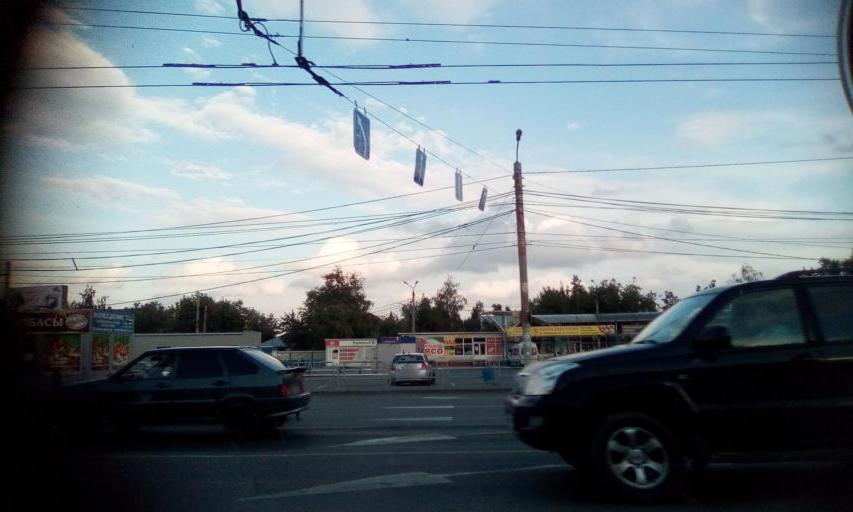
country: RU
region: Chelyabinsk
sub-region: Gorod Chelyabinsk
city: Chelyabinsk
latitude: 55.1361
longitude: 61.3747
